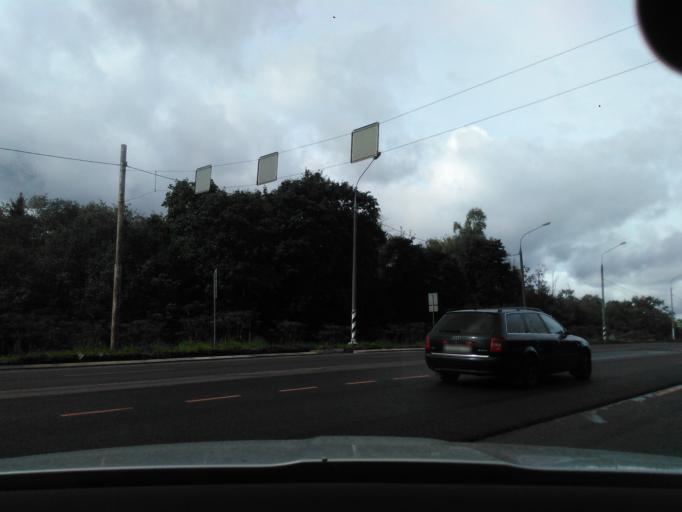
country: RU
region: Moskovskaya
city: Peshki
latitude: 56.1224
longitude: 37.0778
